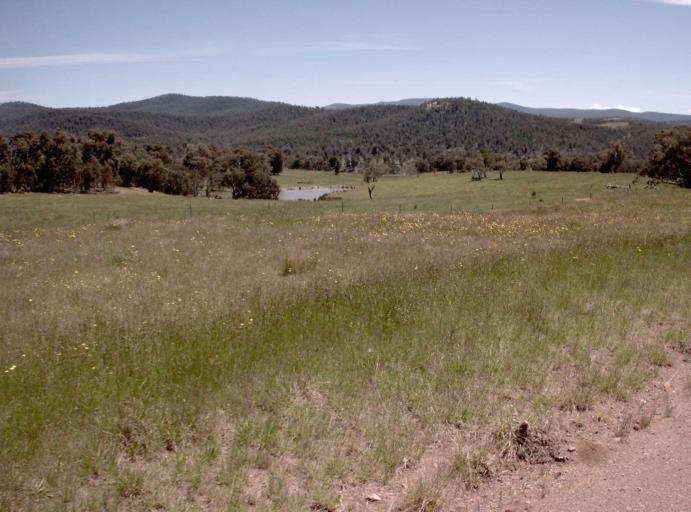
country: AU
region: New South Wales
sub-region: Snowy River
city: Jindabyne
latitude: -37.0826
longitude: 148.2588
